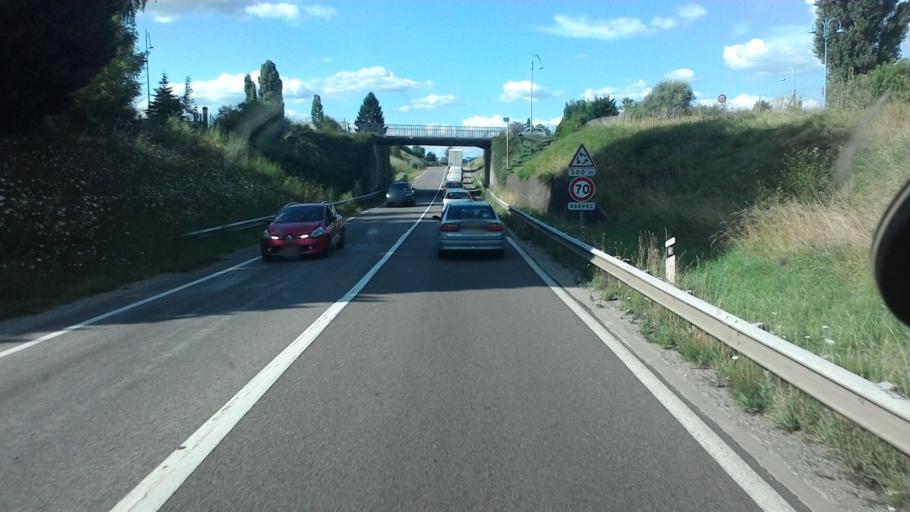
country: FR
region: Franche-Comte
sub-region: Departement de la Haute-Saone
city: Noidans-les-Vesoul
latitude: 47.6117
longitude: 6.1328
